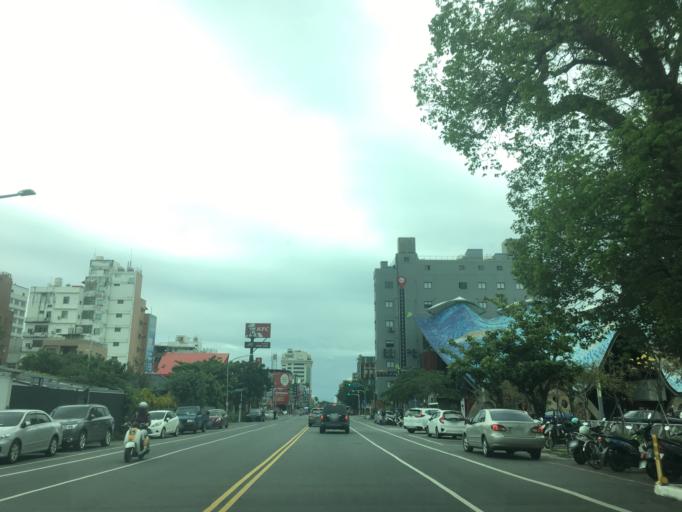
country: TW
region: Taiwan
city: Taitung City
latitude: 22.7537
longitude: 121.1468
